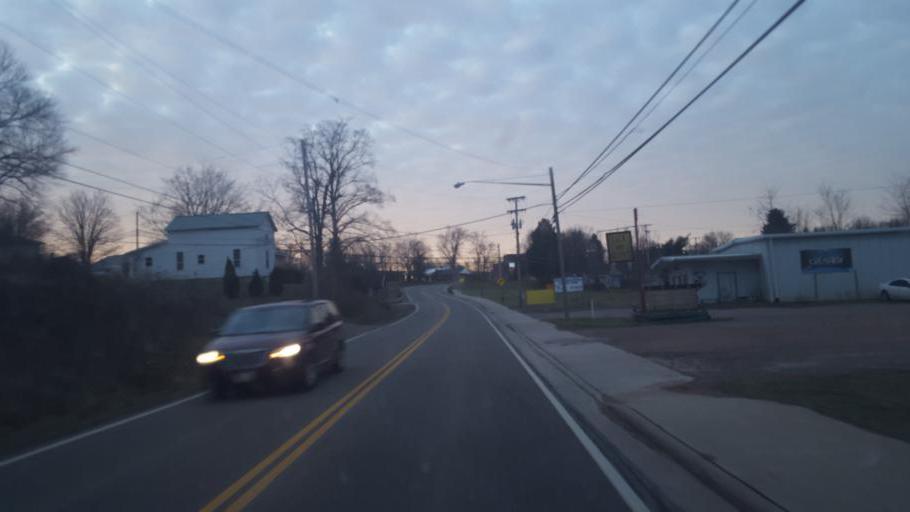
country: US
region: Ohio
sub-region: Jackson County
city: Oak Hill
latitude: 38.8852
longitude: -82.3819
